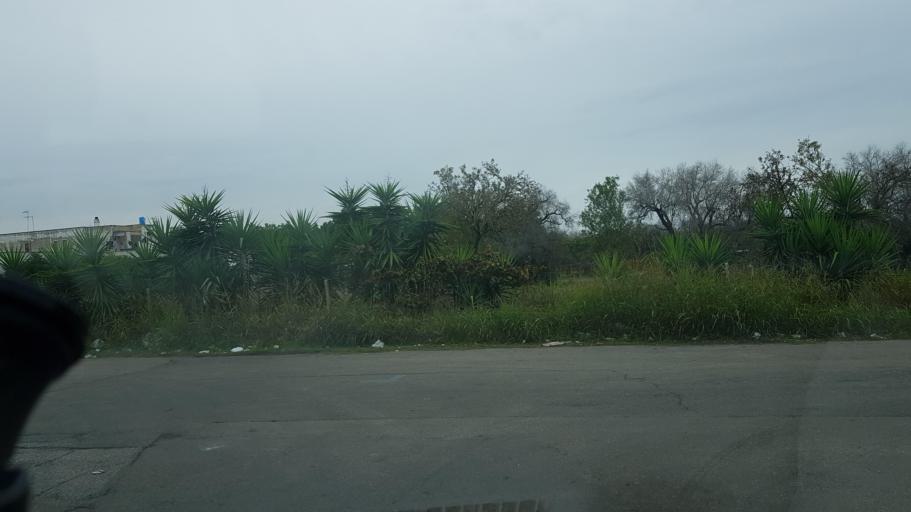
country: IT
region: Apulia
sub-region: Provincia di Brindisi
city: Cellino San Marco
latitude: 40.4761
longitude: 17.9693
